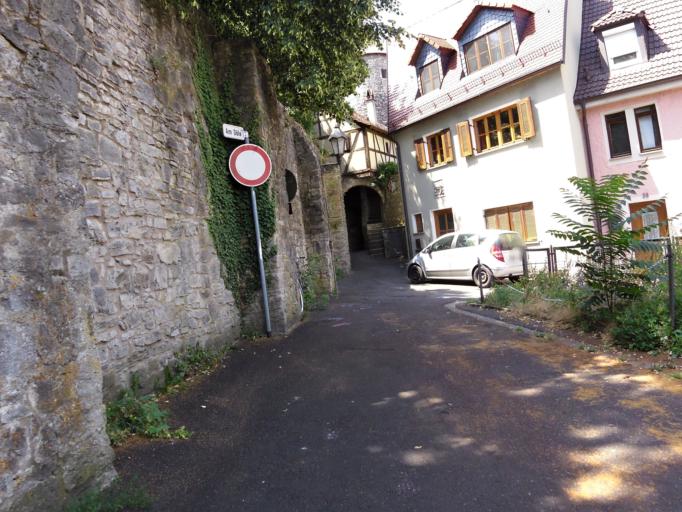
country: DE
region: Bavaria
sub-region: Regierungsbezirk Unterfranken
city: Wuerzburg
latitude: 49.7630
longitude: 9.9479
